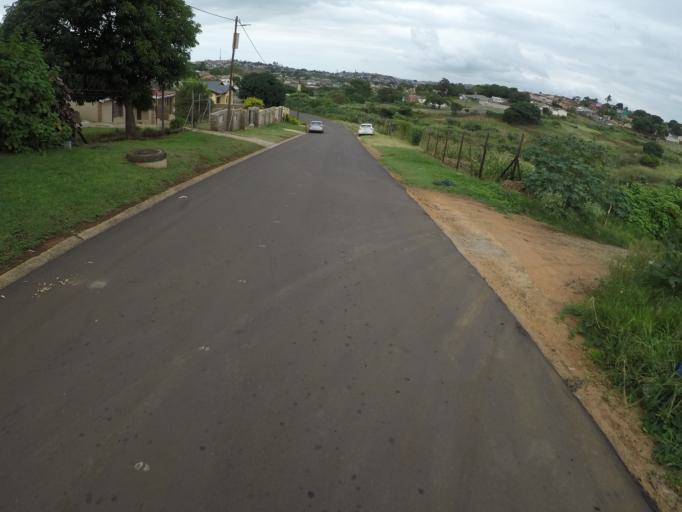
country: ZA
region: KwaZulu-Natal
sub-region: uThungulu District Municipality
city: Empangeni
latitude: -28.7723
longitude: 31.8608
